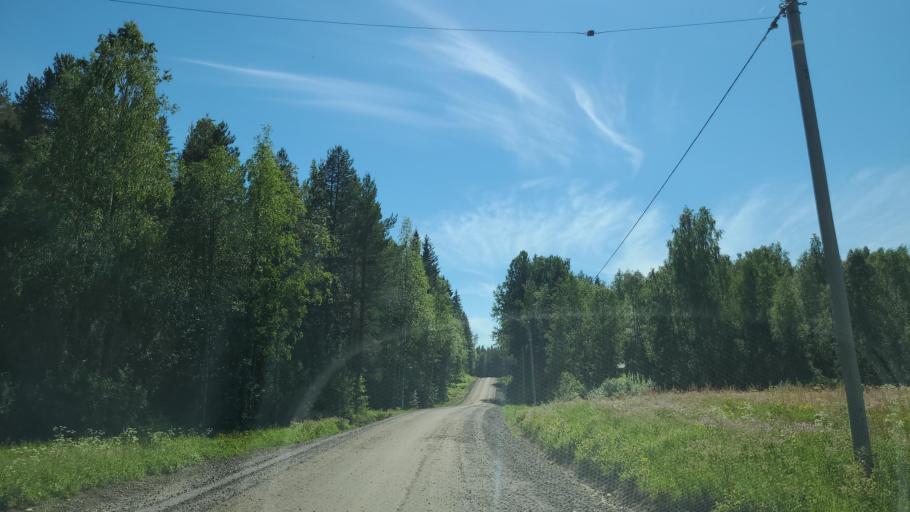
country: SE
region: Vaesterbotten
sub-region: Bjurholms Kommun
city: Bjurholm
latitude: 63.6627
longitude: 19.0792
